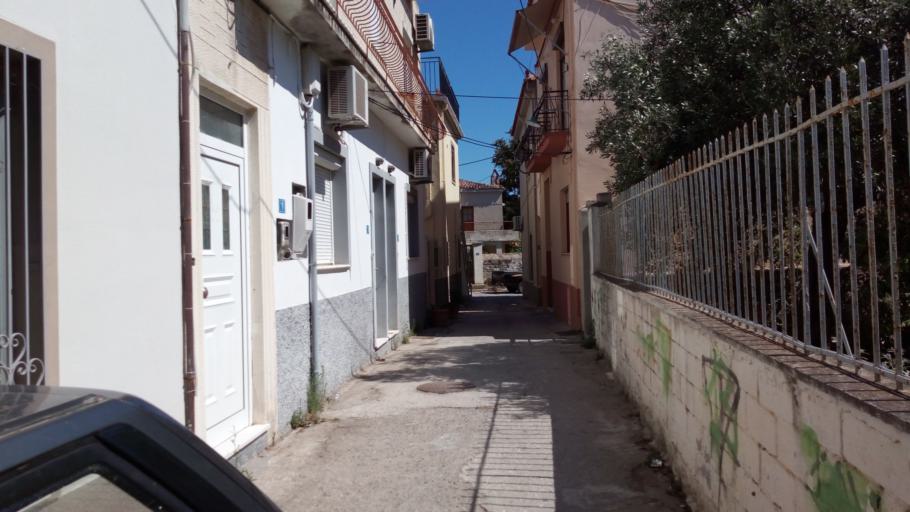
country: GR
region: North Aegean
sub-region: Nomos Lesvou
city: Myrina
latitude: 39.8753
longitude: 25.0603
